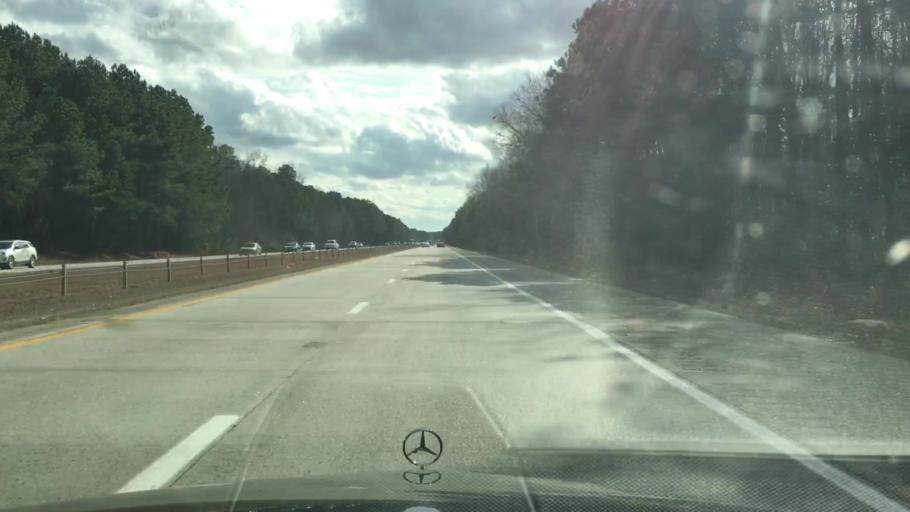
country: US
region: North Carolina
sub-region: Johnston County
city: Benson
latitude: 35.5015
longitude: -78.5544
